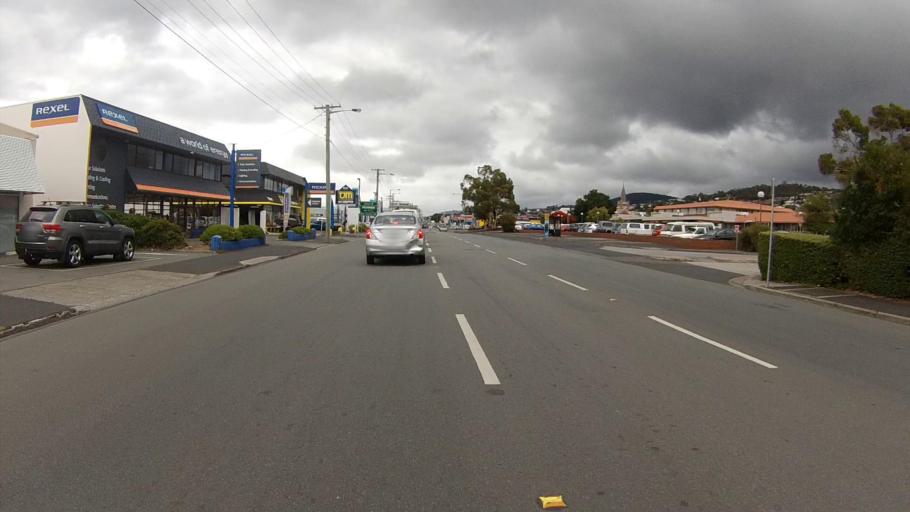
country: AU
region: Tasmania
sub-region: Glenorchy
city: Goodwood
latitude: -42.8385
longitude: 147.2891
